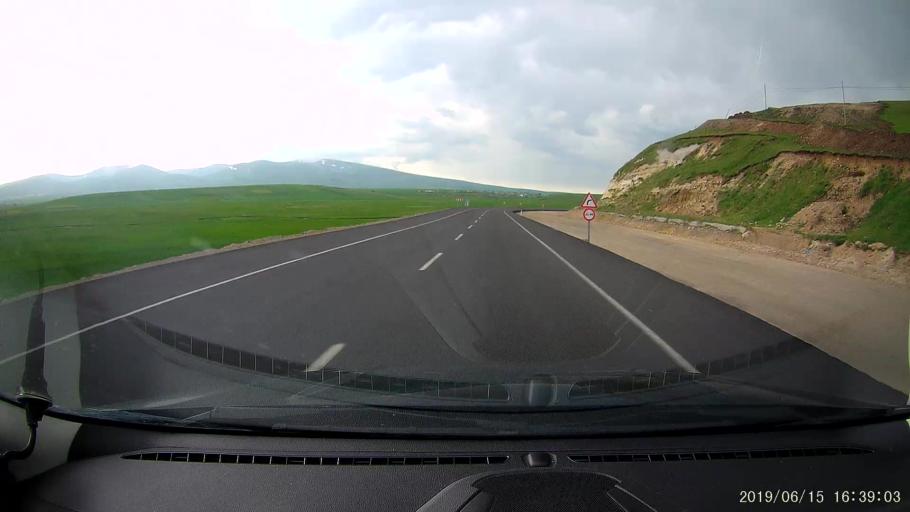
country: TR
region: Ardahan
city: Haskoy
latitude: 40.9869
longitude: 42.8937
